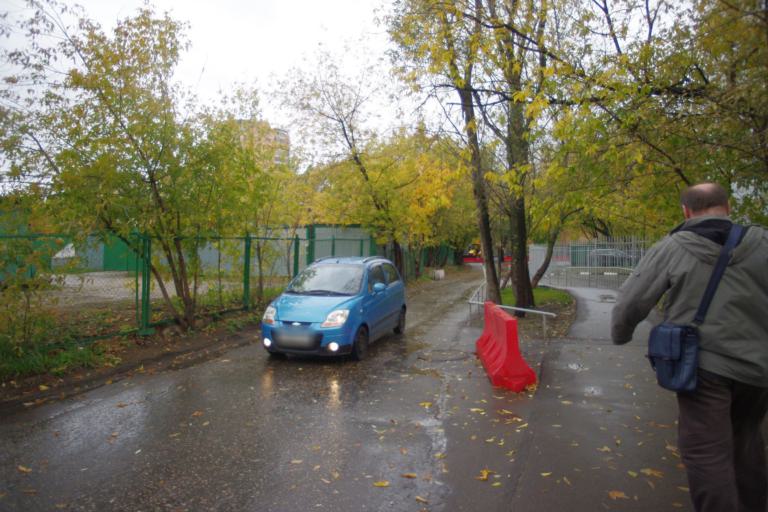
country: RU
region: Moskovskaya
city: Leninskiye Gory
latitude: 55.6925
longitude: 37.5737
